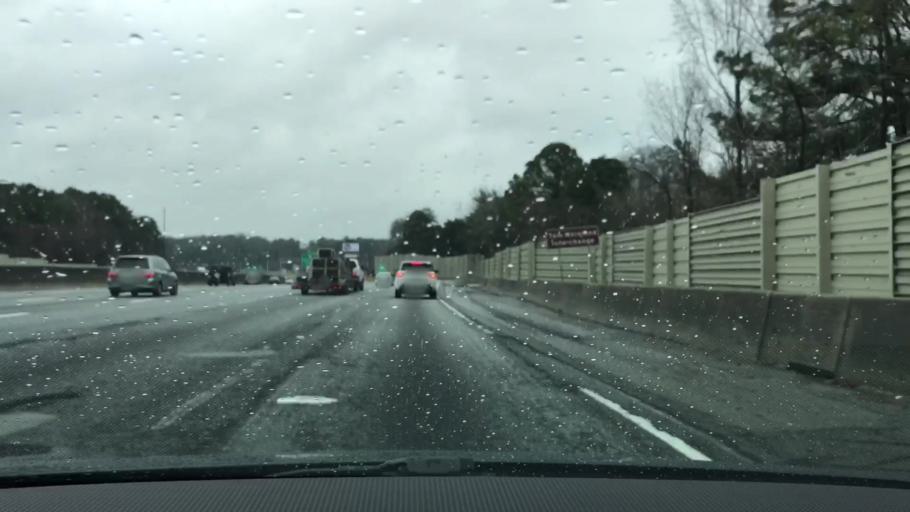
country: US
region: Georgia
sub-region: DeKalb County
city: Doraville
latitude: 33.8787
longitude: -84.2490
